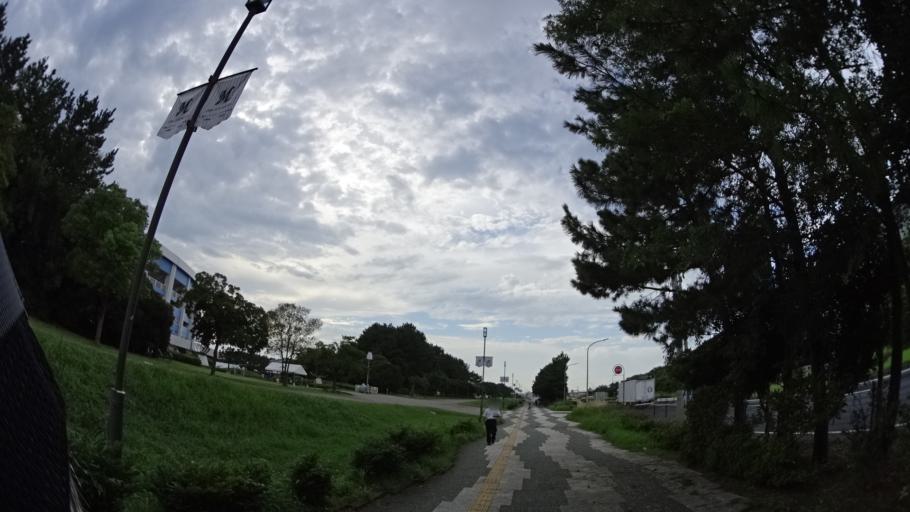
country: JP
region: Chiba
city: Funabashi
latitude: 35.6462
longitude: 140.0328
